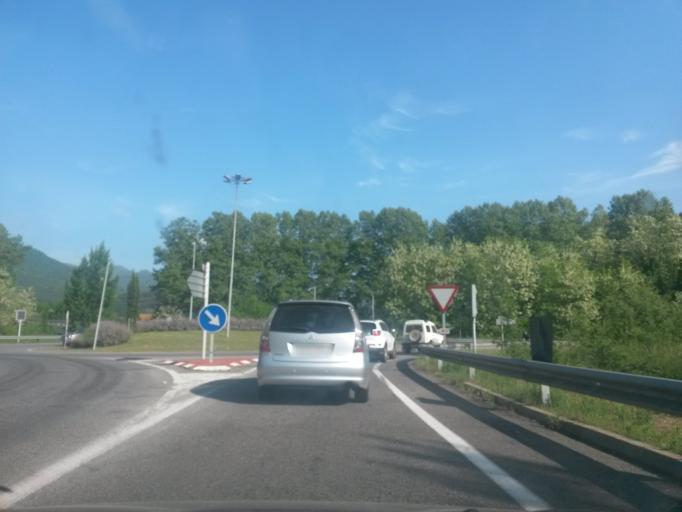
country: ES
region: Catalonia
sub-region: Provincia de Girona
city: Bas
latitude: 42.1282
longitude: 2.4496
